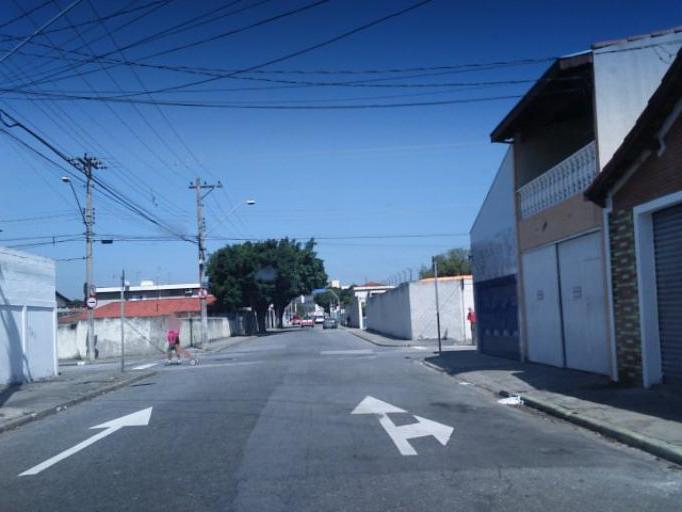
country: BR
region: Sao Paulo
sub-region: Sao Jose Dos Campos
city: Sao Jose dos Campos
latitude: -23.1916
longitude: -45.8790
